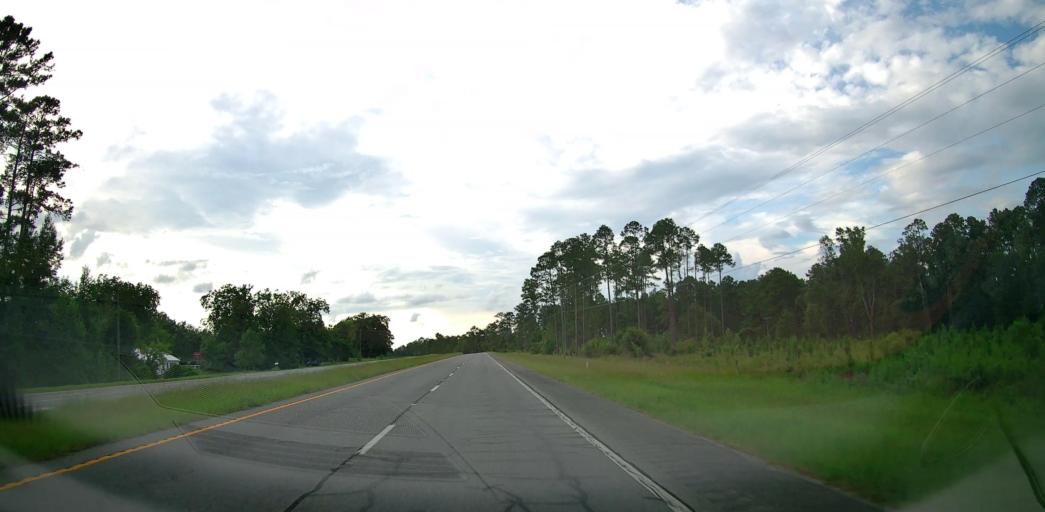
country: US
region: Georgia
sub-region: Pulaski County
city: Hawkinsville
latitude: 32.2660
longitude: -83.4111
